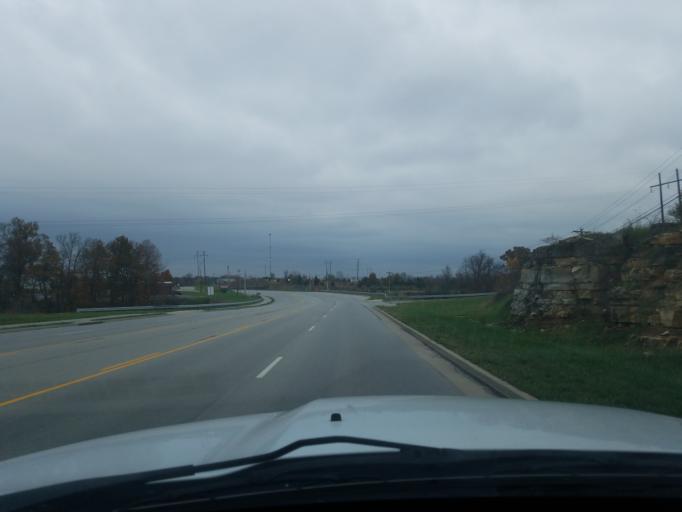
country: US
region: Kentucky
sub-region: Nelson County
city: Bardstown
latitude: 37.8113
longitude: -85.4278
